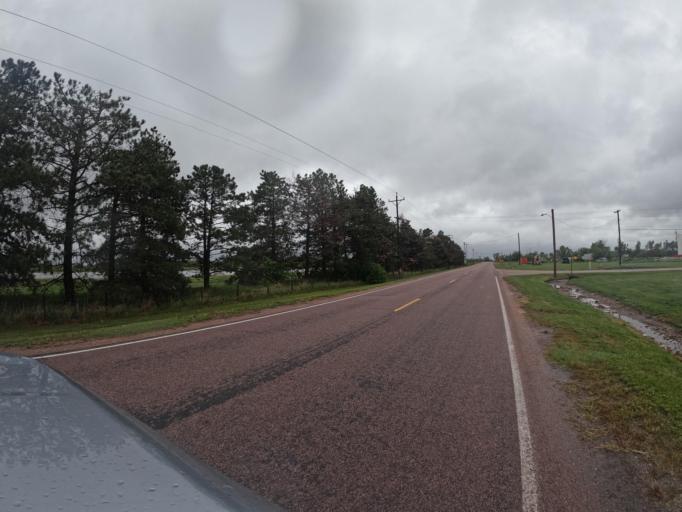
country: US
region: Nebraska
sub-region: Clay County
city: Harvard
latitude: 40.6184
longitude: -98.0898
